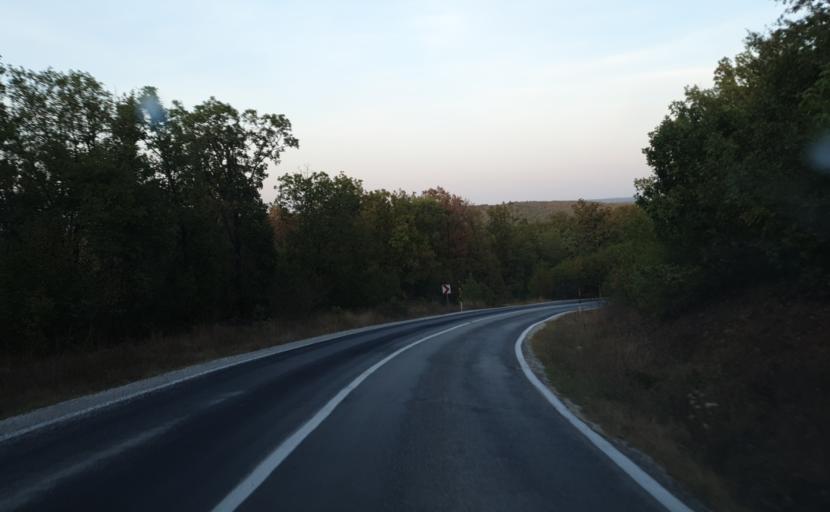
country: TR
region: Kirklareli
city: Igneada
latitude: 41.8798
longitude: 27.8895
